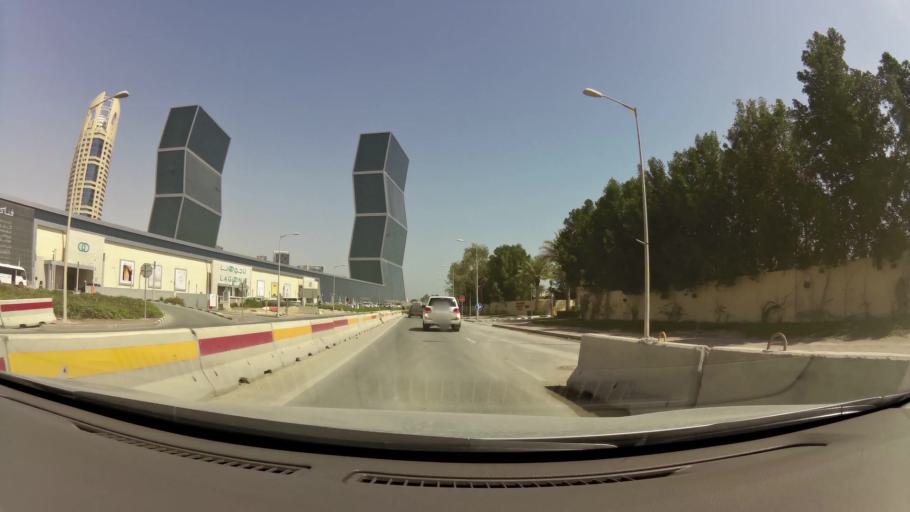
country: QA
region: Baladiyat ad Dawhah
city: Doha
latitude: 25.3747
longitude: 51.5256
